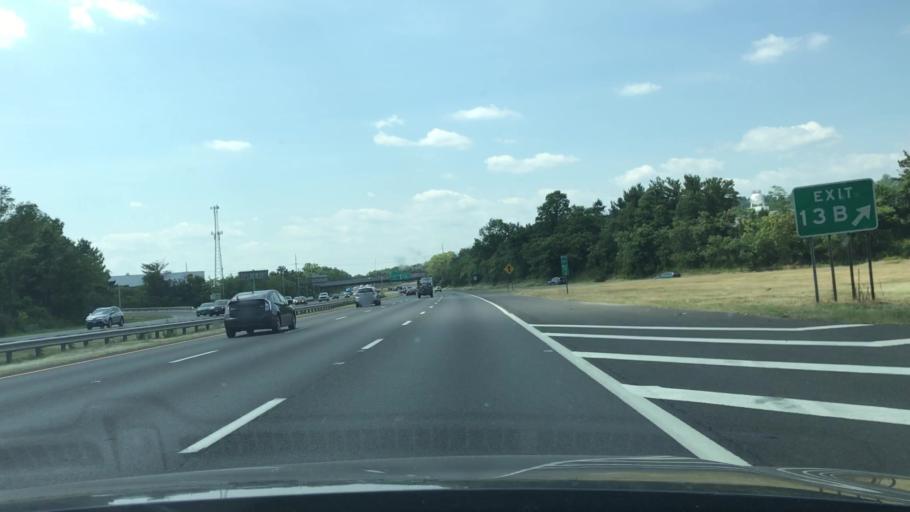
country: US
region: New Jersey
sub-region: Somerset County
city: Bound Brook
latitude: 40.5684
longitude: -74.5570
